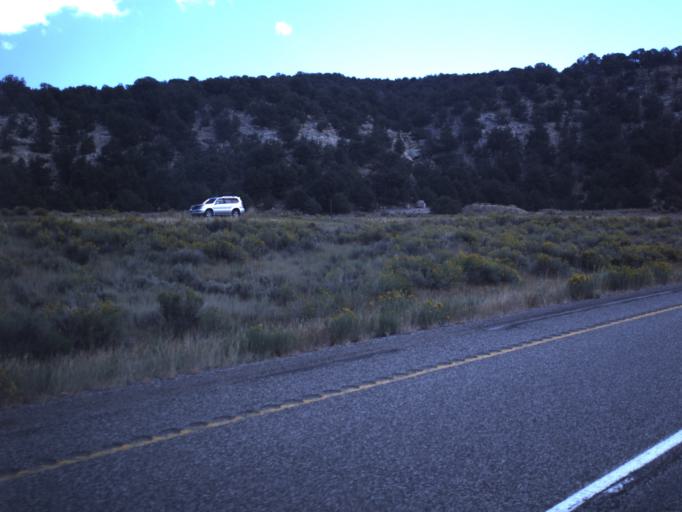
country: US
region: Utah
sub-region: Sevier County
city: Salina
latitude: 38.8503
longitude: -111.5430
